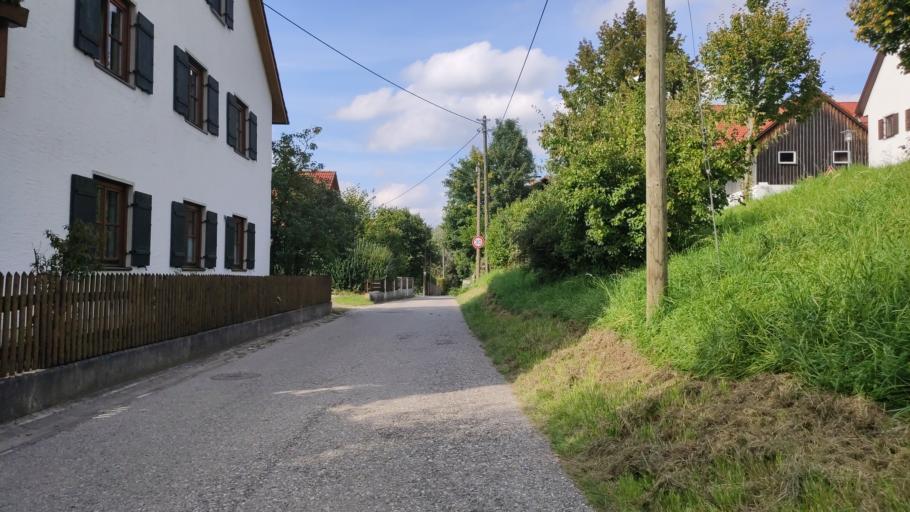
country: DE
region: Bavaria
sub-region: Upper Bavaria
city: Kaufering
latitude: 48.0942
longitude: 10.8742
